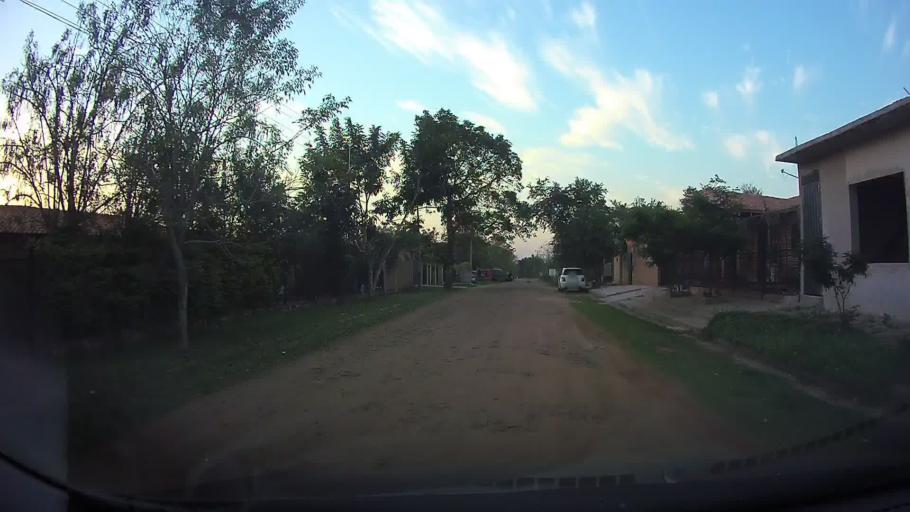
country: PY
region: Central
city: Limpio
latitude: -25.2330
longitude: -57.4689
